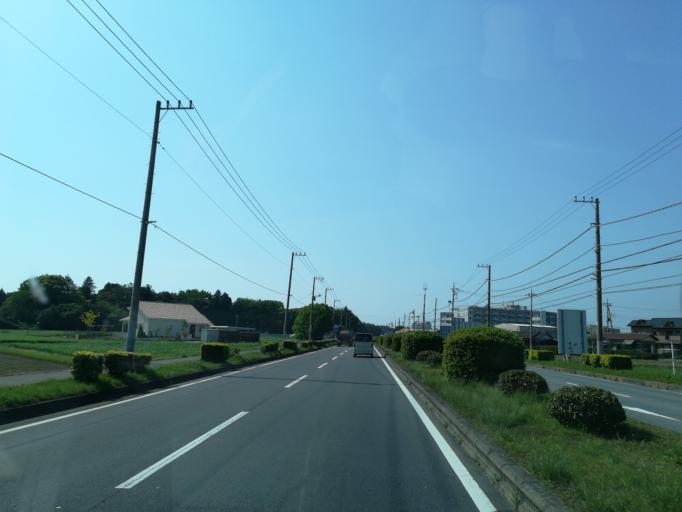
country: JP
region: Ibaraki
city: Tsukuba
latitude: 36.1045
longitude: 140.0829
